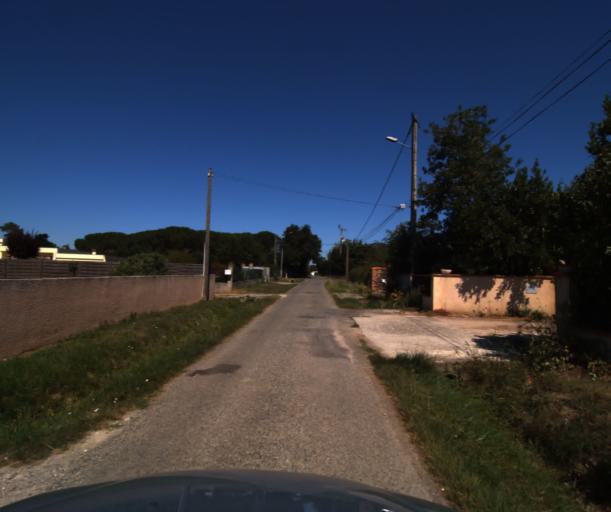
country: FR
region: Midi-Pyrenees
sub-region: Departement de la Haute-Garonne
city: Muret
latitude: 43.4553
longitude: 1.3604
